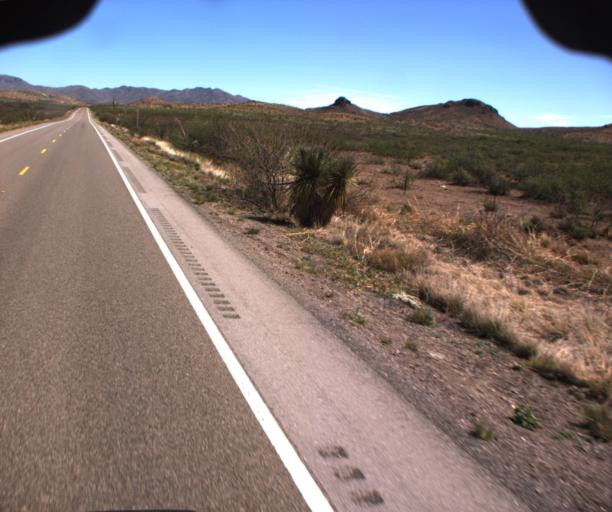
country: US
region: Arizona
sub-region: Cochise County
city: Douglas
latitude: 31.4632
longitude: -109.4546
